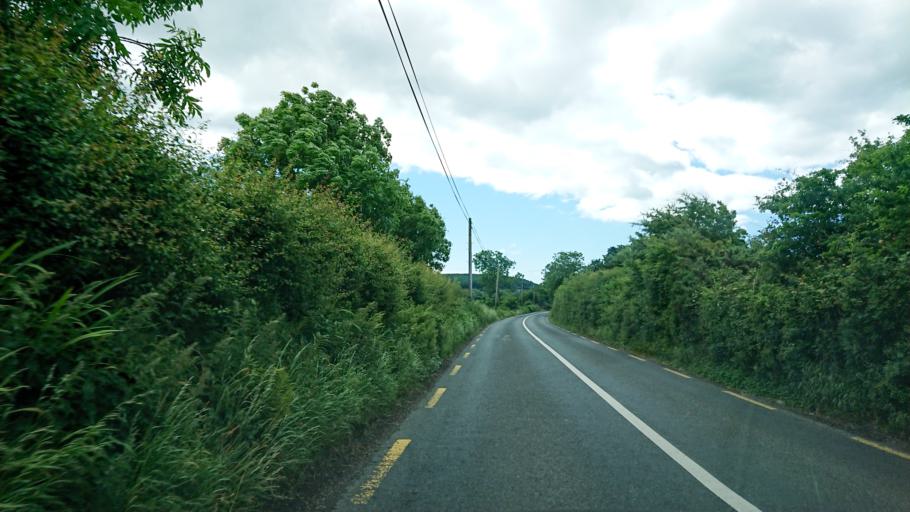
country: IE
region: Munster
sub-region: Waterford
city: Tra Mhor
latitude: 52.1911
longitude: -7.1824
